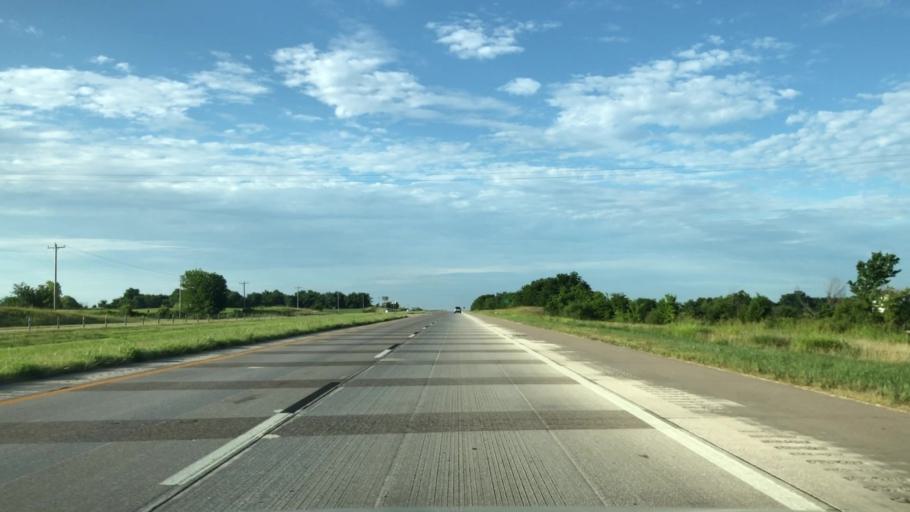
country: US
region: Oklahoma
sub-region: Osage County
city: Skiatook
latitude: 36.4327
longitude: -95.9207
